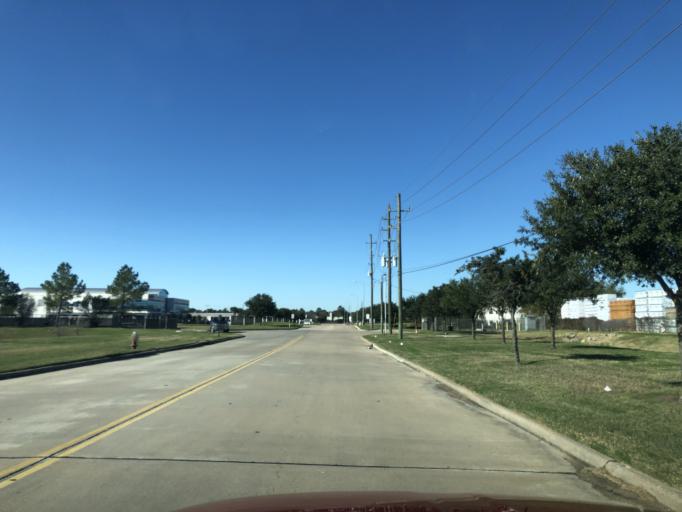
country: US
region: Texas
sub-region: Harris County
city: Oak Cliff Place
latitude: 29.9362
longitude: -95.6551
